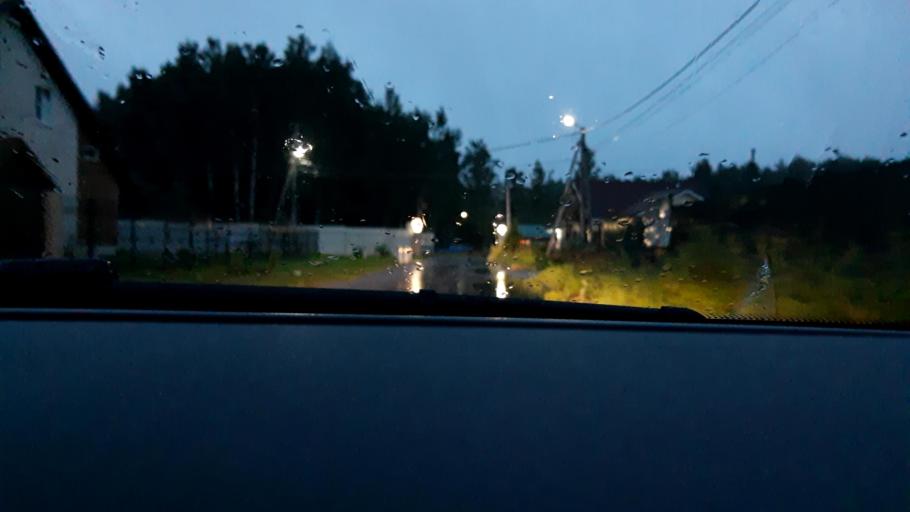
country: RU
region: Nizjnij Novgorod
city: Burevestnik
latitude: 56.0520
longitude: 43.9533
